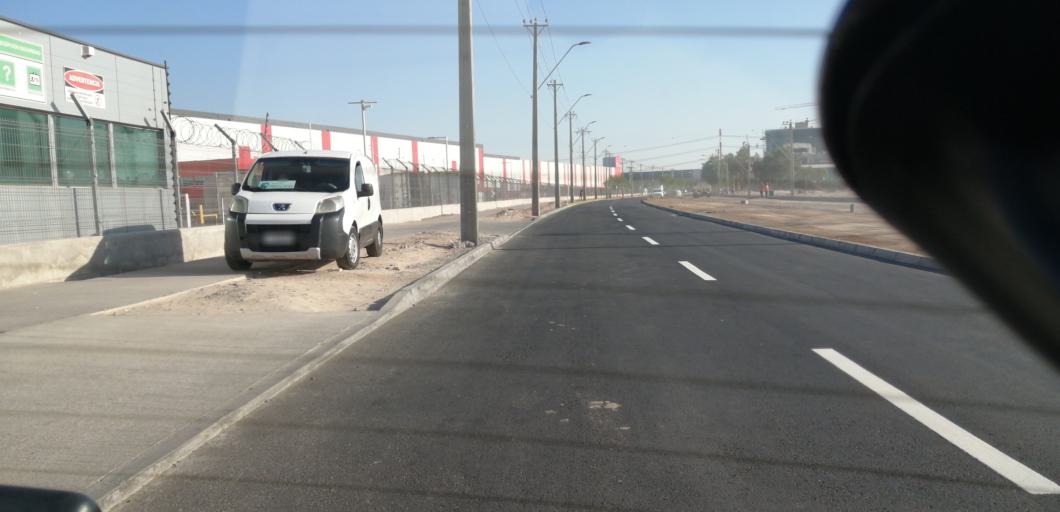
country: CL
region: Santiago Metropolitan
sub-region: Provincia de Santiago
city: Lo Prado
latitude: -33.4366
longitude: -70.7879
